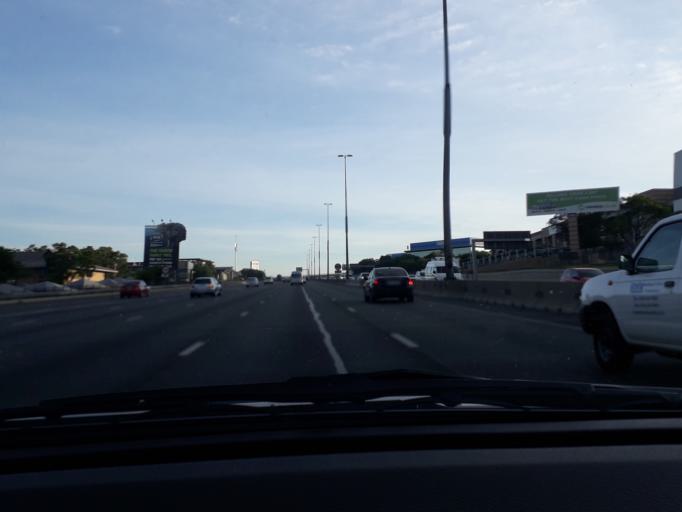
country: ZA
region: Gauteng
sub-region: City of Johannesburg Metropolitan Municipality
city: Midrand
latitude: -26.0135
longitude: 28.1166
